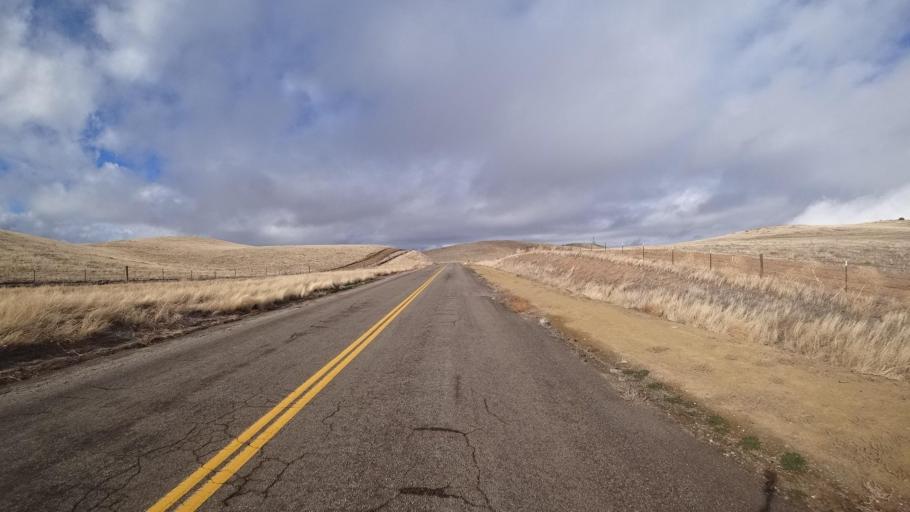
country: US
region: California
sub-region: Kern County
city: Maricopa
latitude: 34.9073
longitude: -119.3872
